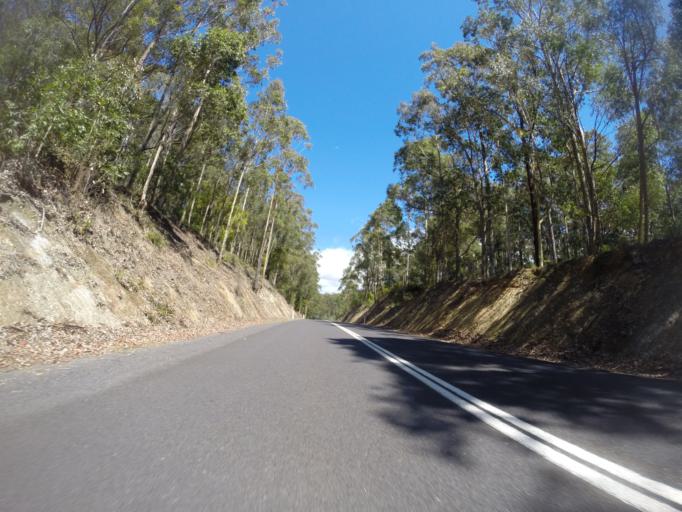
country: AU
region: New South Wales
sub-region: Eurobodalla
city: Batemans Bay
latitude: -35.6573
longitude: 150.2769
